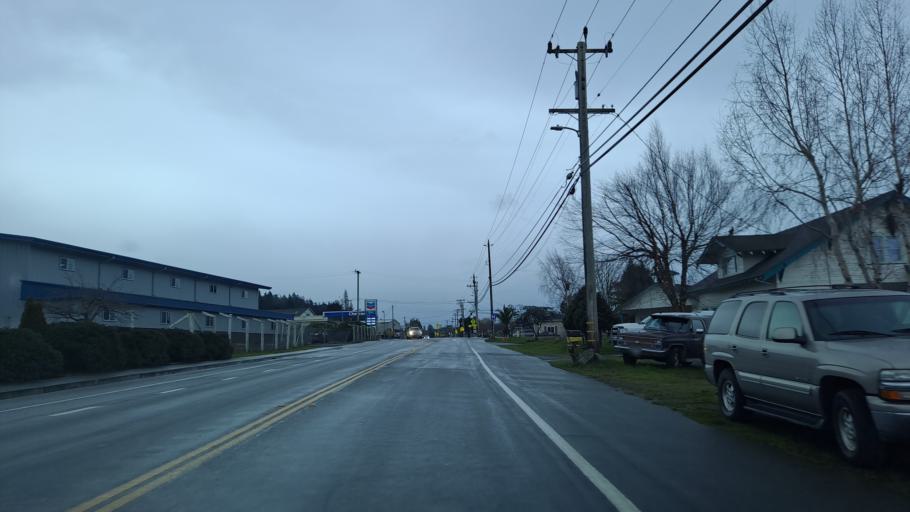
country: US
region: California
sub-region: Humboldt County
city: Fortuna
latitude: 40.5840
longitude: -124.1312
